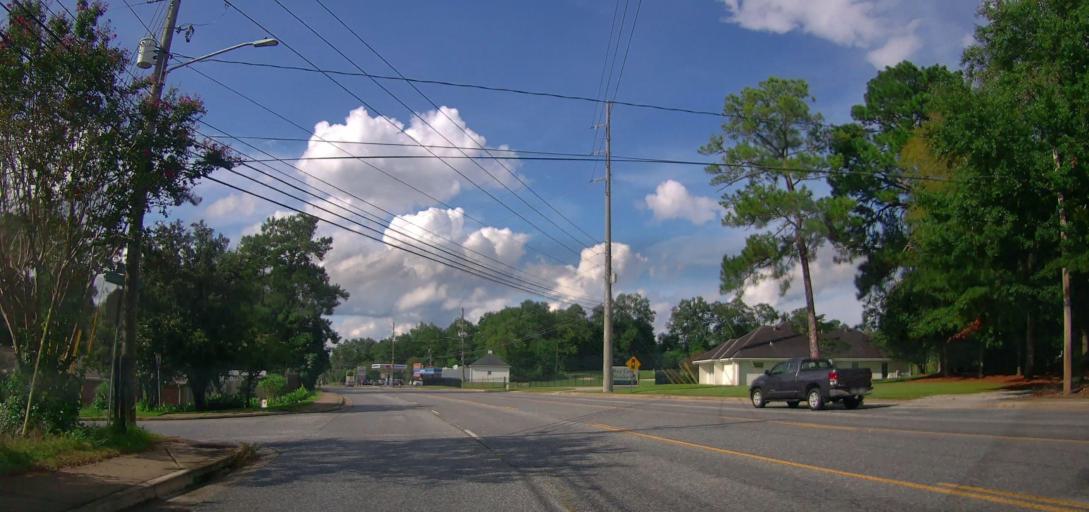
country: US
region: Georgia
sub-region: Muscogee County
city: Columbus
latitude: 32.4971
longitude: -84.9324
